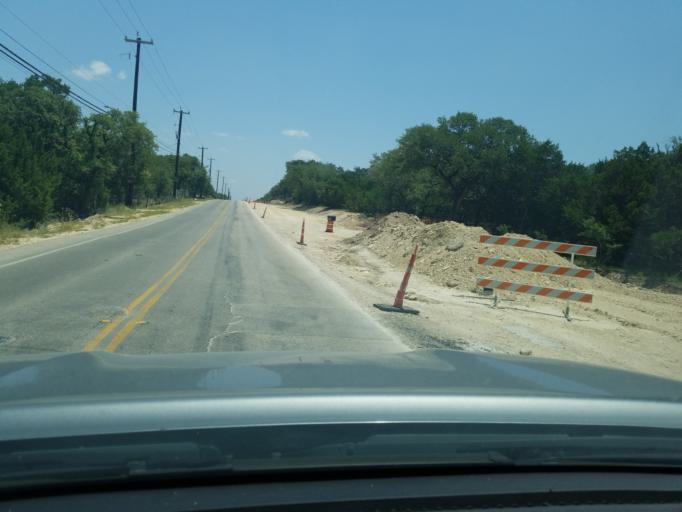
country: US
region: Texas
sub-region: Bexar County
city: Timberwood Park
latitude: 29.7083
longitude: -98.4980
